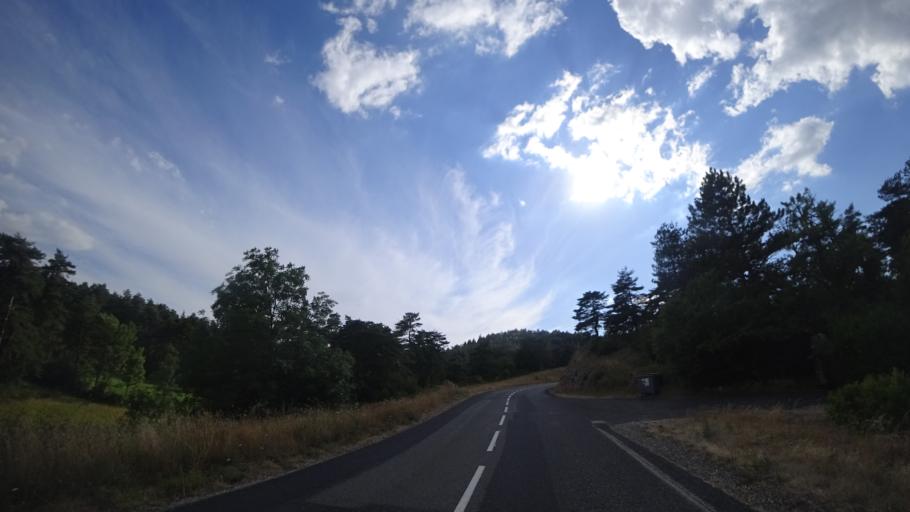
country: FR
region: Languedoc-Roussillon
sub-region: Departement de la Lozere
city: Chanac
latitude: 44.3741
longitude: 3.3344
